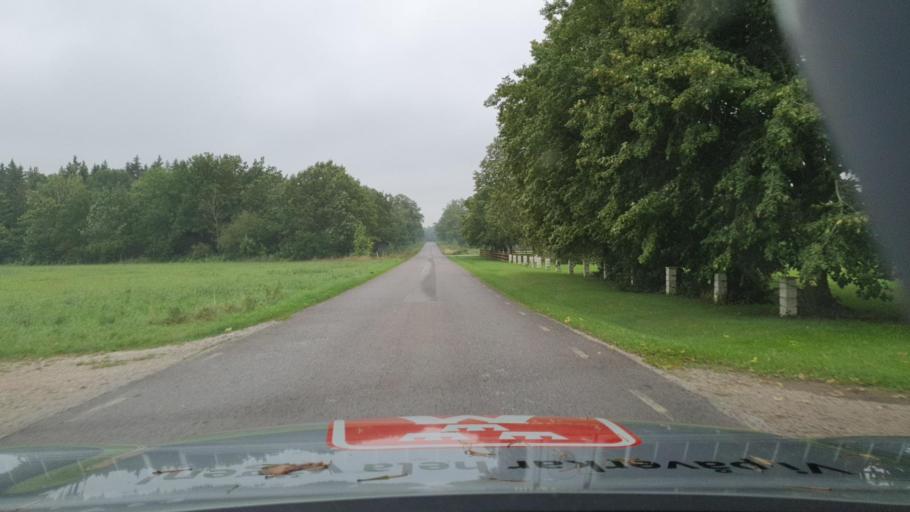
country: SE
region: Gotland
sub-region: Gotland
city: Visby
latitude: 57.7731
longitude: 18.4956
